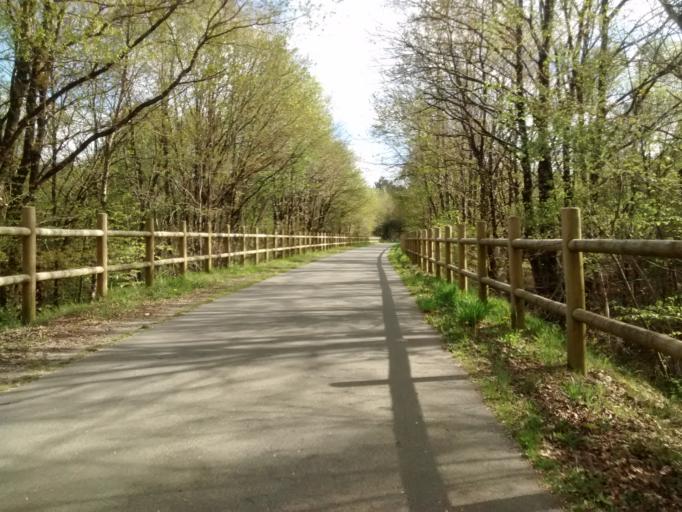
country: FR
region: Brittany
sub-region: Departement du Morbihan
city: Pleucadeuc
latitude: 47.7532
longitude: -2.4011
